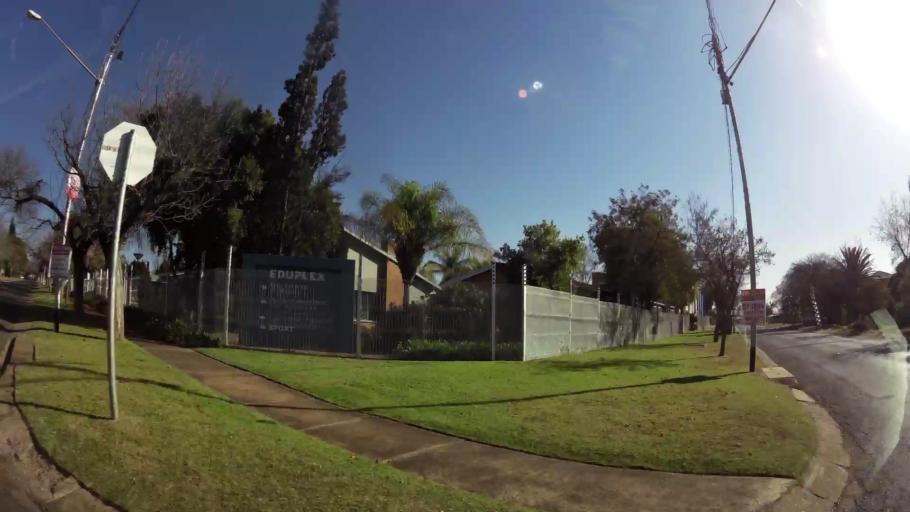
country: ZA
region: Gauteng
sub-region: City of Tshwane Metropolitan Municipality
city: Pretoria
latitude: -25.7227
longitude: 28.2483
